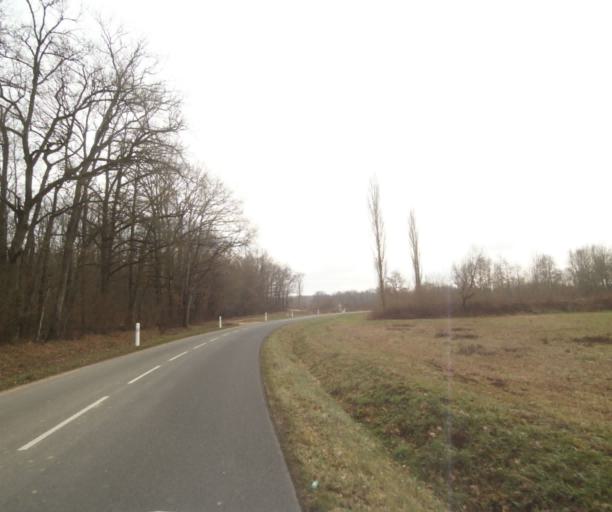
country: FR
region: Champagne-Ardenne
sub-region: Departement de la Marne
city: Pargny-sur-Saulx
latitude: 48.7473
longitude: 4.8615
